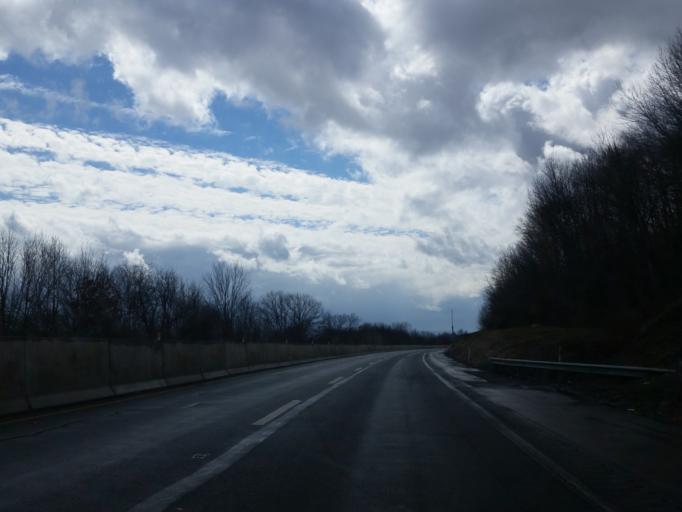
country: US
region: Pennsylvania
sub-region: Lackawanna County
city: Taylor
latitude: 41.4310
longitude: -75.7046
